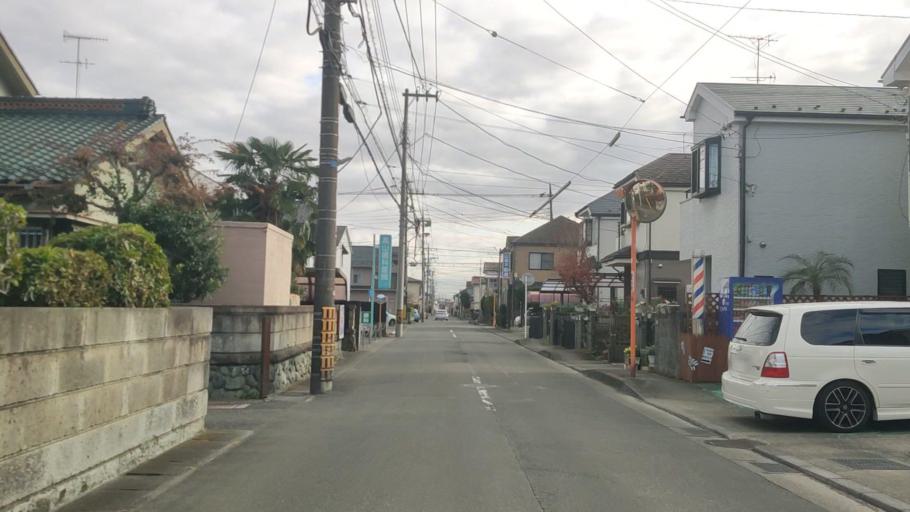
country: JP
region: Kanagawa
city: Minami-rinkan
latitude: 35.4915
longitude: 139.4442
